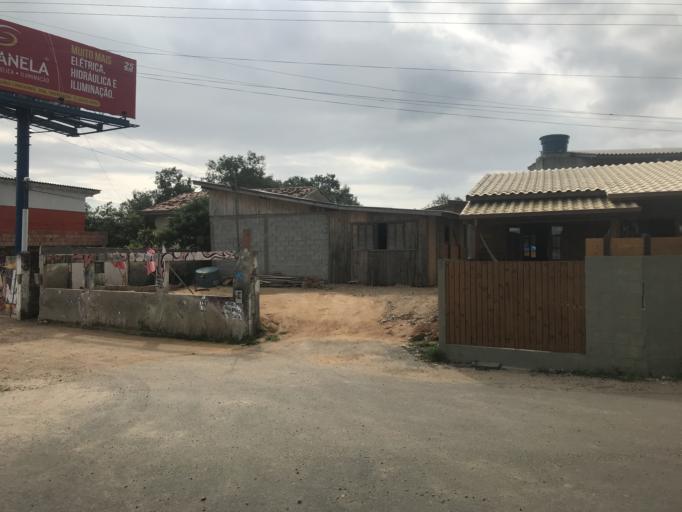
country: BR
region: Santa Catarina
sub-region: Florianopolis
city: Costeira do Pirajubae
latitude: -27.6505
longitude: -48.5225
